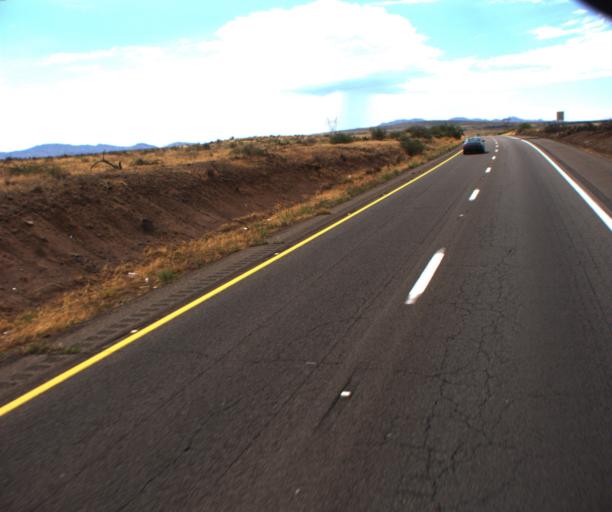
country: US
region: Arizona
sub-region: Yavapai County
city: Cordes Lakes
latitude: 34.2261
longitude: -112.1148
